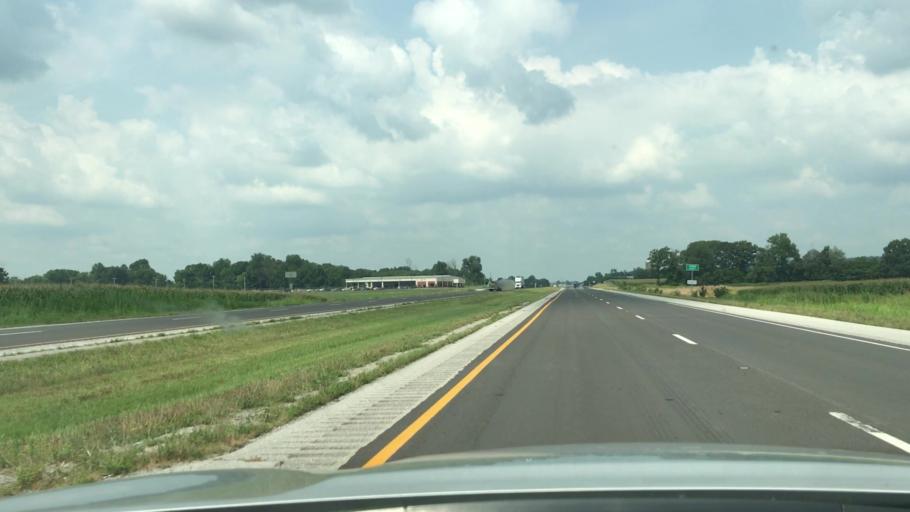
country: US
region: Kentucky
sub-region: Todd County
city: Elkton
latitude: 36.8055
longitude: -87.0578
